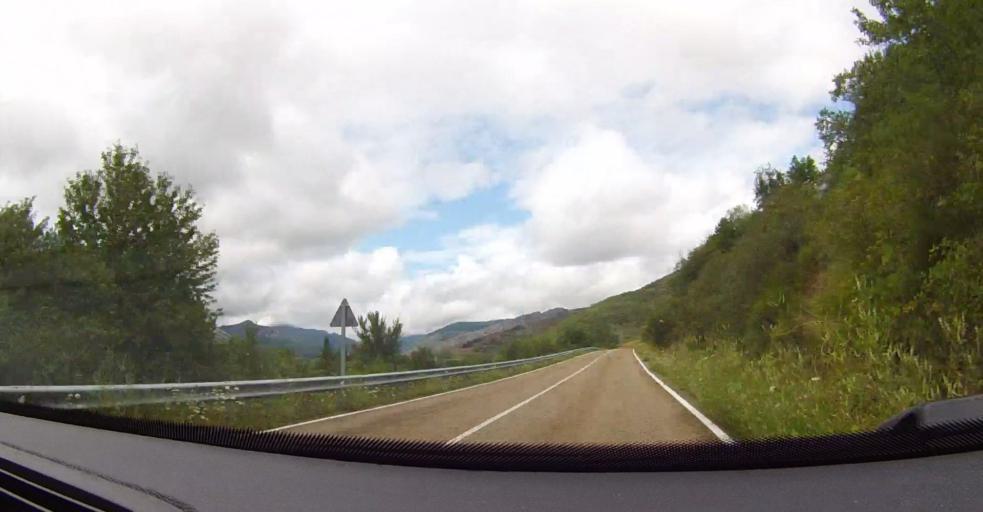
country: ES
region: Castille and Leon
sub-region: Provincia de Leon
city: Puebla de Lillo
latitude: 42.9809
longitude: -5.2554
